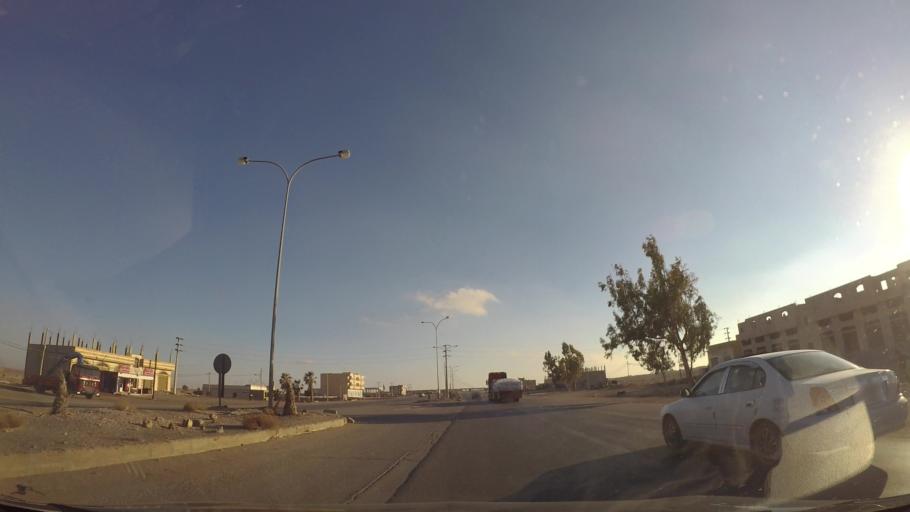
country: JO
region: Tafielah
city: Busayra
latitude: 30.5864
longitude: 35.8014
